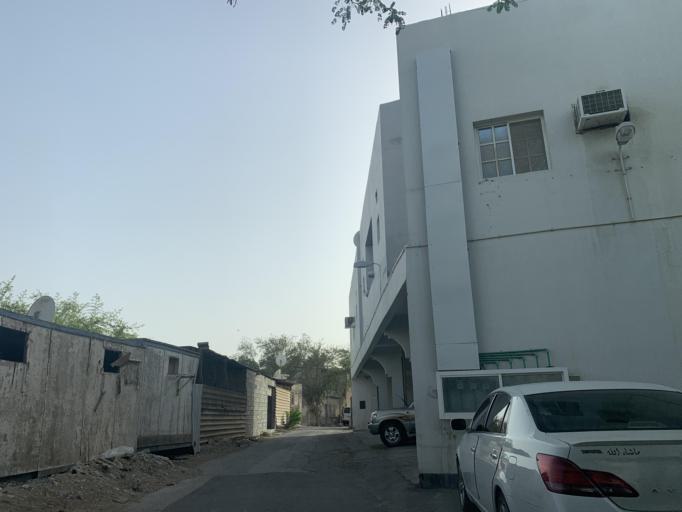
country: BH
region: Northern
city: Madinat `Isa
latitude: 26.1603
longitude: 50.5143
